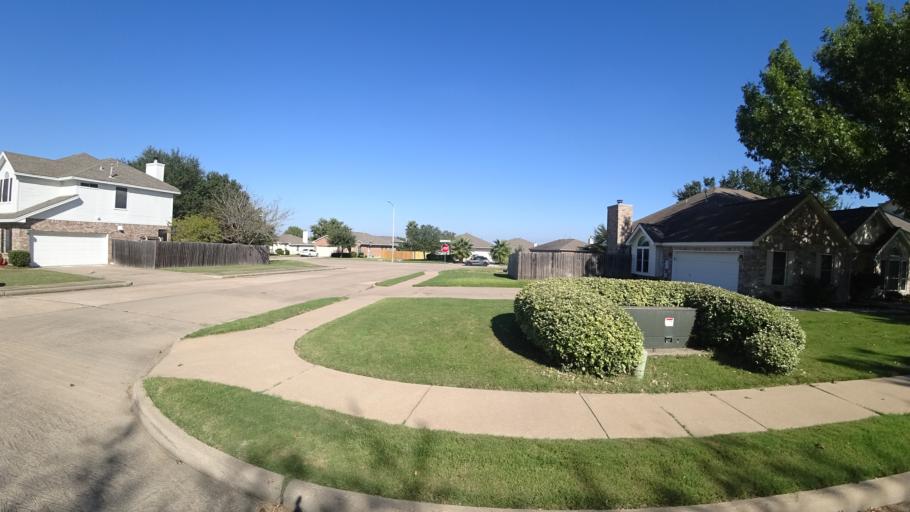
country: US
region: Texas
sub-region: Travis County
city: Manor
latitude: 30.3552
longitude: -97.6137
